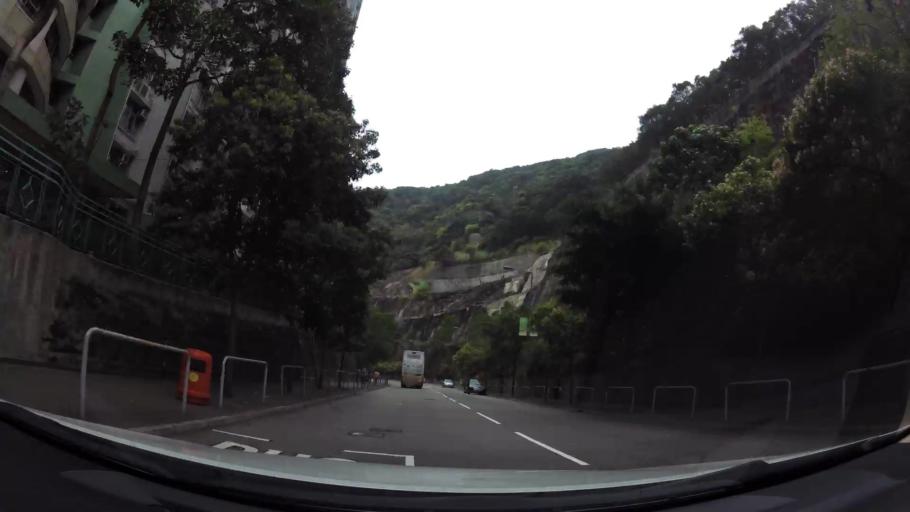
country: HK
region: Wanchai
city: Wan Chai
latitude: 22.2764
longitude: 114.2243
